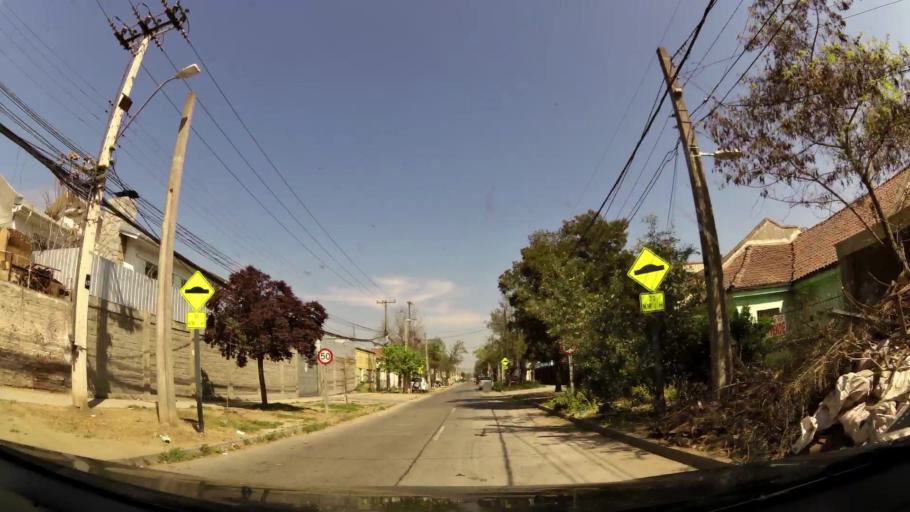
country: CL
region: Santiago Metropolitan
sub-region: Provincia de Santiago
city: Santiago
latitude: -33.4041
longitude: -70.6698
